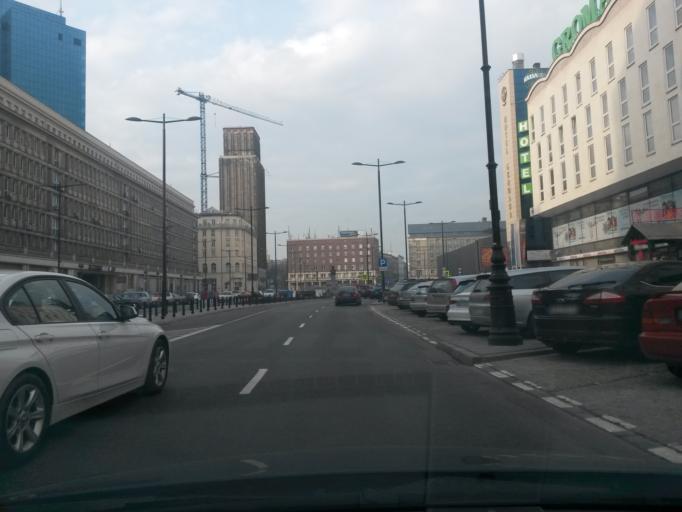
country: PL
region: Masovian Voivodeship
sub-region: Warszawa
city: Warsaw
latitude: 52.2338
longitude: 21.0142
